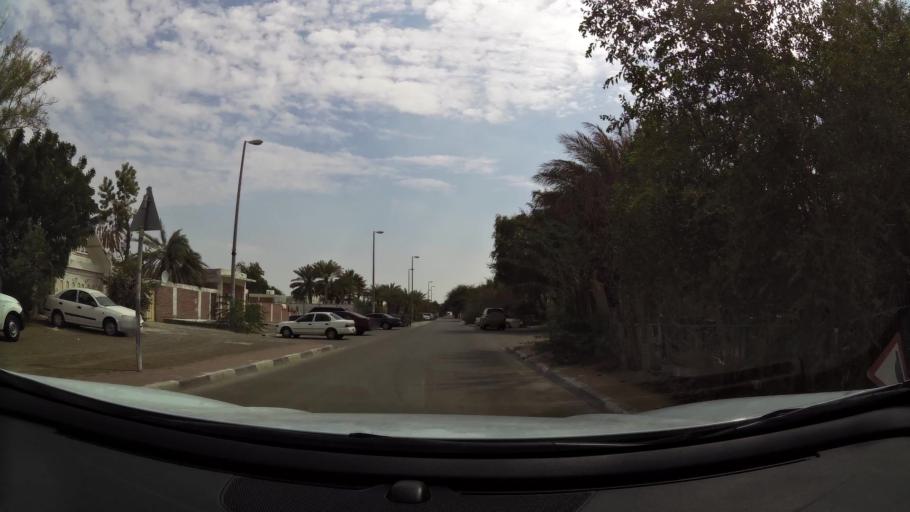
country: AE
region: Abu Dhabi
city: Al Ain
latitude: 24.1971
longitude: 55.7921
